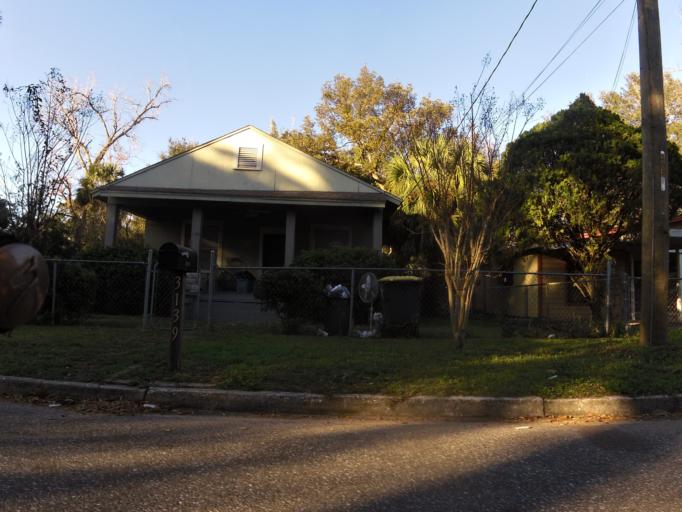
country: US
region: Florida
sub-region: Duval County
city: Jacksonville
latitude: 30.3191
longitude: -81.7088
